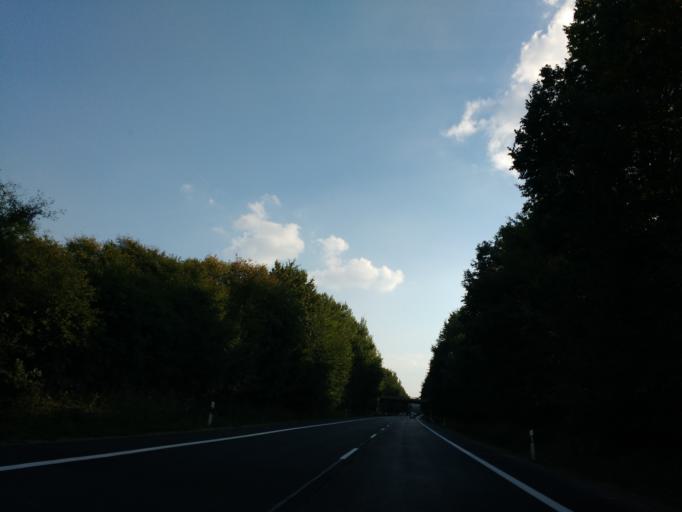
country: DE
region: North Rhine-Westphalia
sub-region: Regierungsbezirk Detmold
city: Blomberg
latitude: 51.9260
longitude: 9.0863
